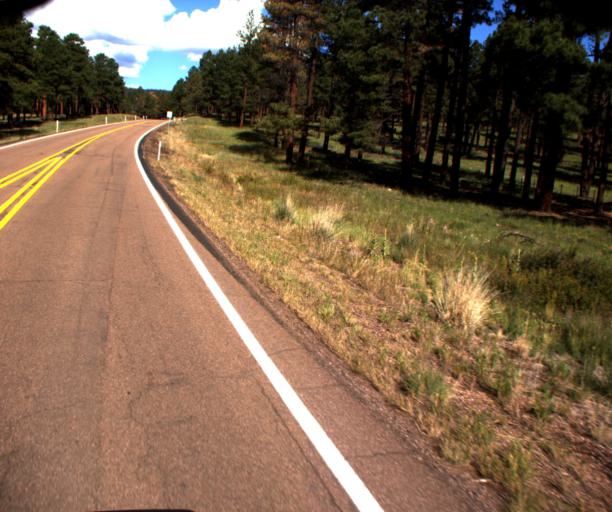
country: US
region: Arizona
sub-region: Apache County
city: Eagar
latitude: 34.0760
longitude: -109.4681
